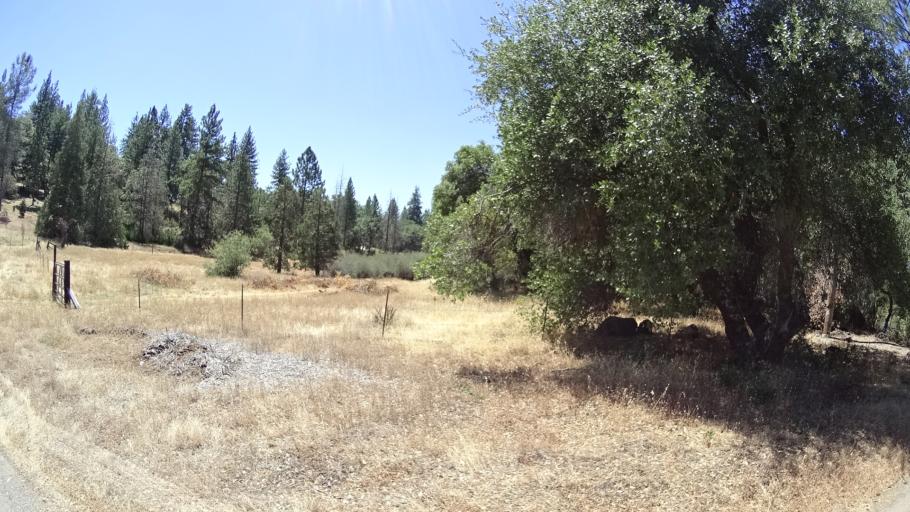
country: US
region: California
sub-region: Calaveras County
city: Forest Meadows
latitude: 38.1358
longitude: -120.4011
